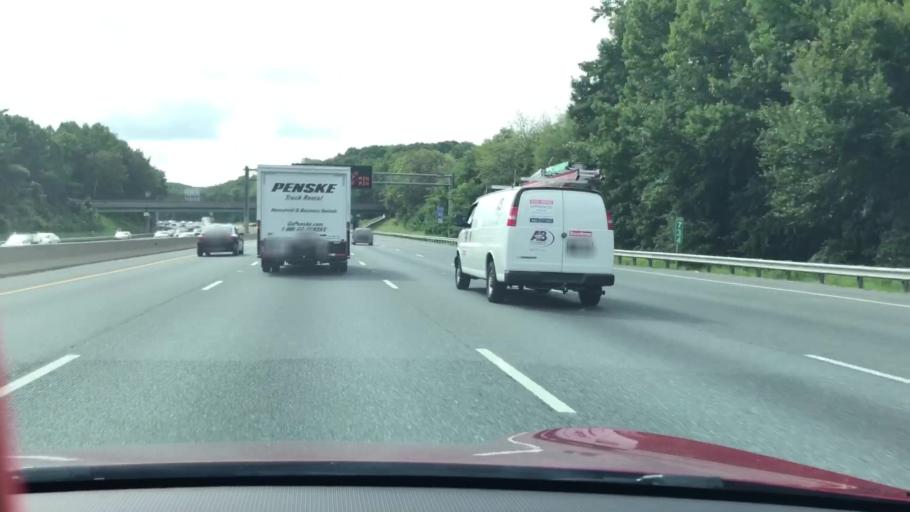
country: US
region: Maryland
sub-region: Harford County
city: Joppatowne
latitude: 39.4426
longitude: -76.3626
